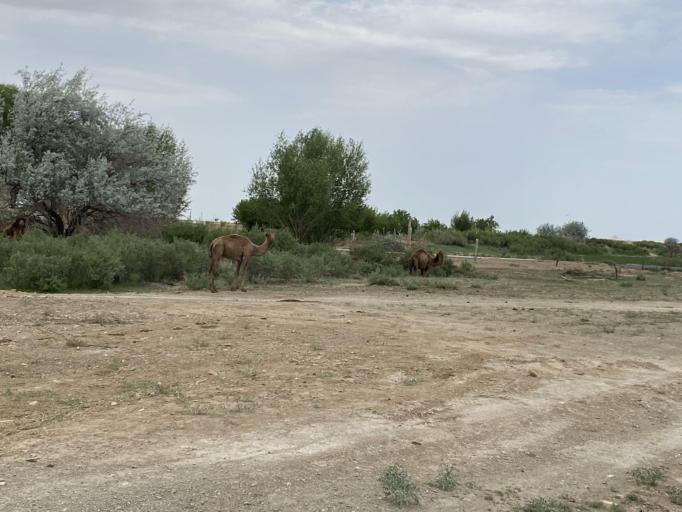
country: KZ
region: Ongtustik Qazaqstan
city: Kentau
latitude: 44.1034
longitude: 68.3814
